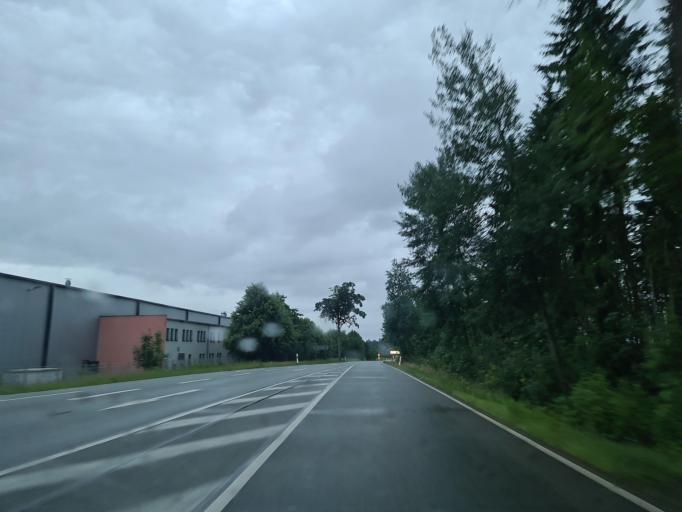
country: DE
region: Saxony
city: Limbach
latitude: 50.5446
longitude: 12.2589
